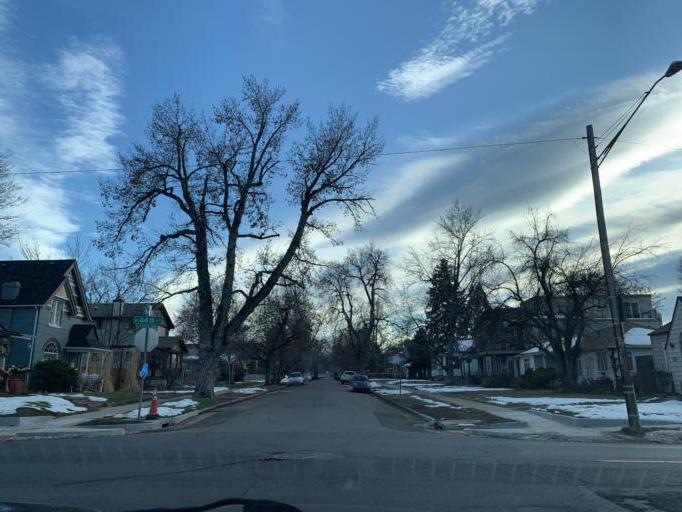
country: US
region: Colorado
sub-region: Jefferson County
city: Edgewater
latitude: 39.7767
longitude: -105.0487
